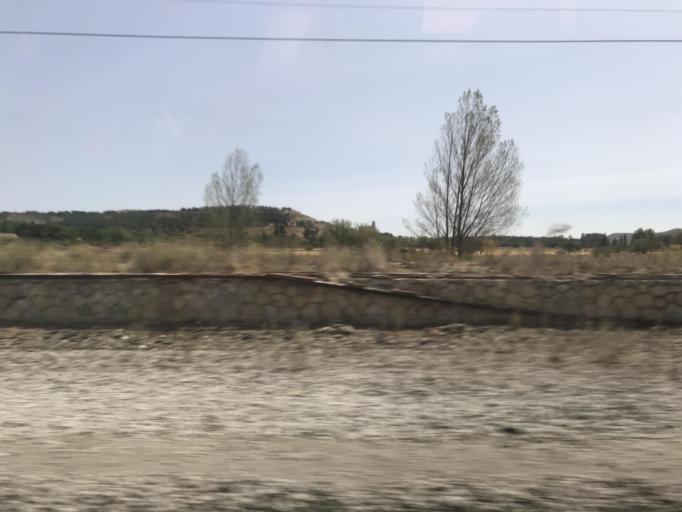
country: ES
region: Castille and Leon
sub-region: Provincia de Burgos
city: Villaquiran de los Infantes
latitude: 42.2148
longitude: -4.0005
